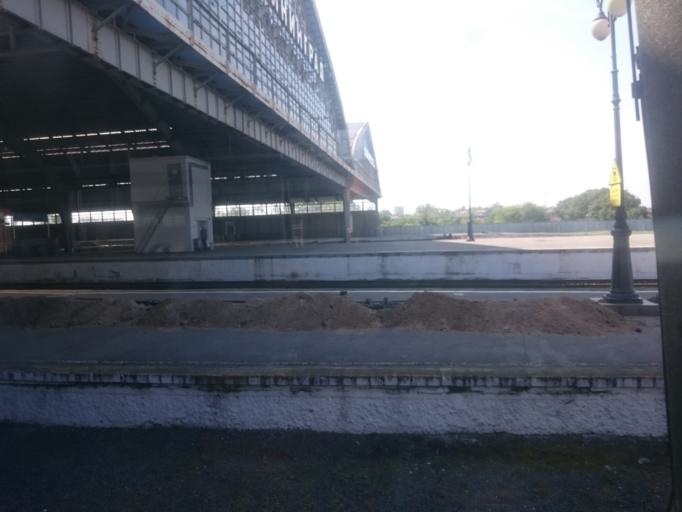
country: RU
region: Kaliningrad
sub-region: Gorod Kaliningrad
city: Kaliningrad
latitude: 54.6940
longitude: 20.4976
